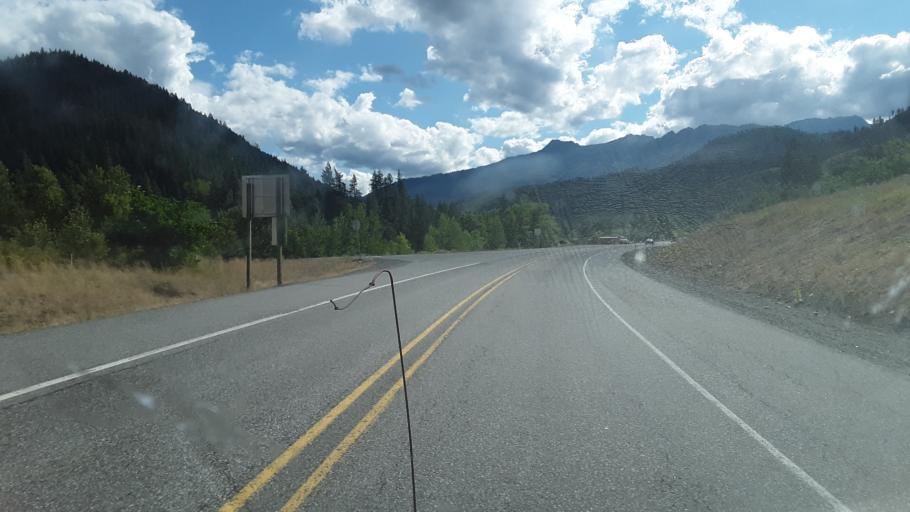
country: US
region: Washington
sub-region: Chelan County
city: Leavenworth
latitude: 47.5568
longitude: -120.5956
